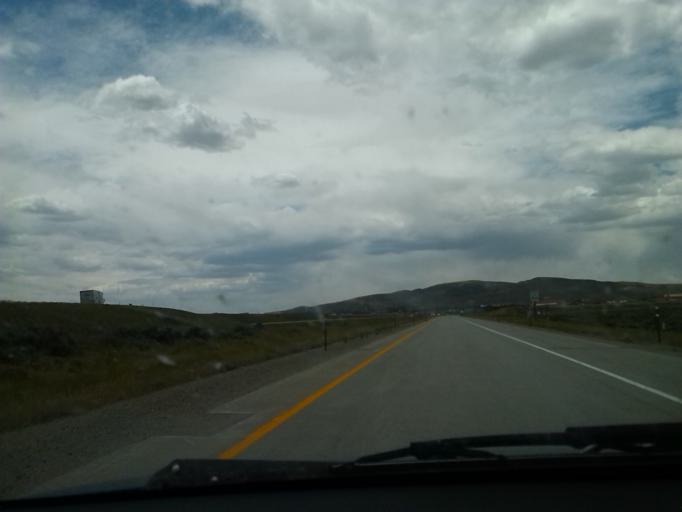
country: US
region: Wyoming
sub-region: Carbon County
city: Rawlins
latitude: 41.7899
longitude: -107.1975
